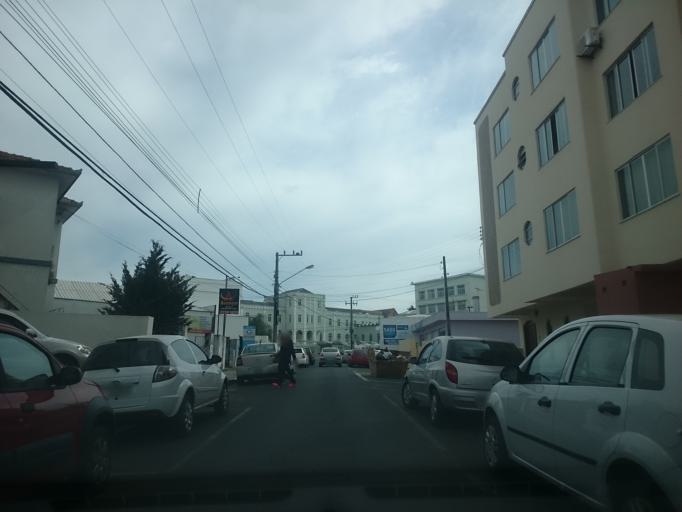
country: BR
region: Santa Catarina
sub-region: Lages
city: Lages
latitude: -27.8190
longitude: -50.3250
